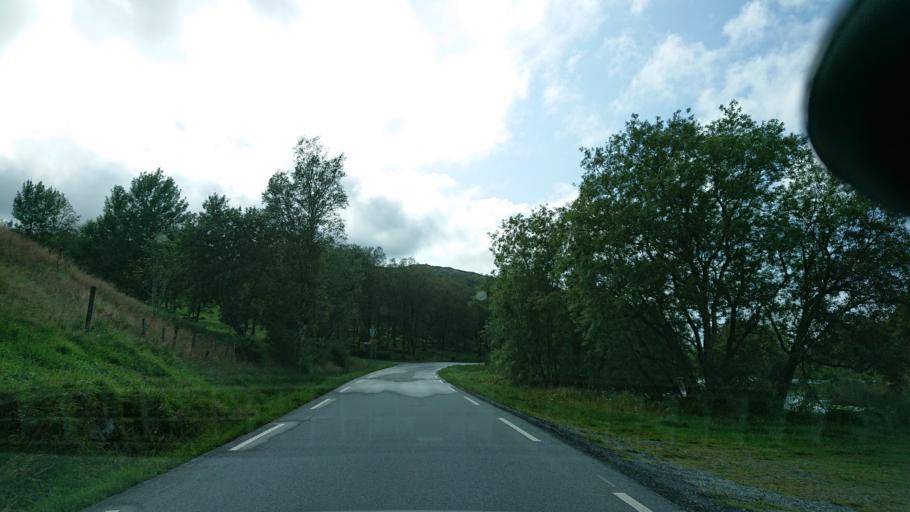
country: NO
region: Rogaland
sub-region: Gjesdal
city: Algard
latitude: 58.6769
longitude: 5.8214
